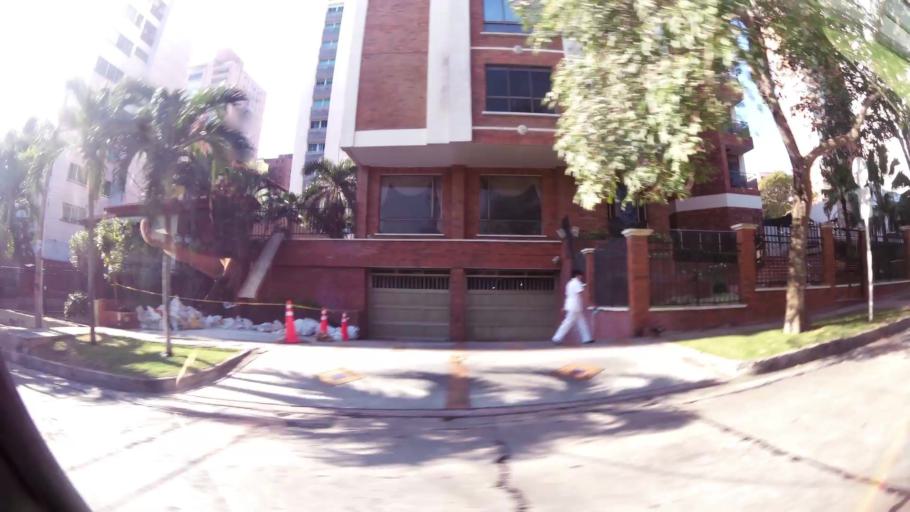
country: CO
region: Atlantico
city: Barranquilla
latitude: 11.0083
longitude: -74.8078
